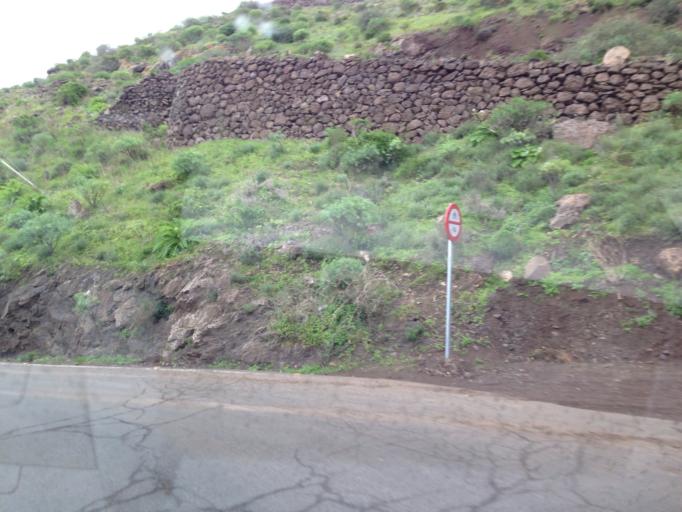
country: ES
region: Canary Islands
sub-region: Provincia de Las Palmas
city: San Nicolas
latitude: 28.0349
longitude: -15.7577
